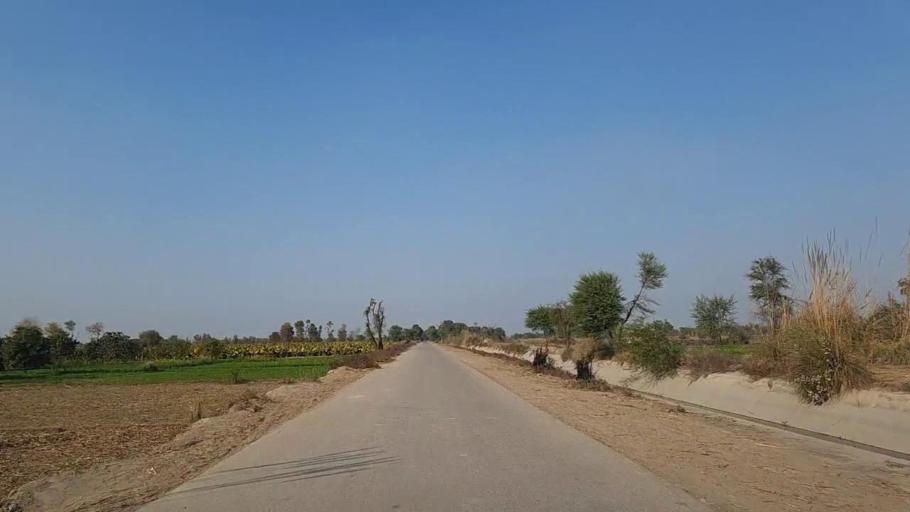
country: PK
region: Sindh
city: Daur
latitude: 26.4077
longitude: 68.2591
